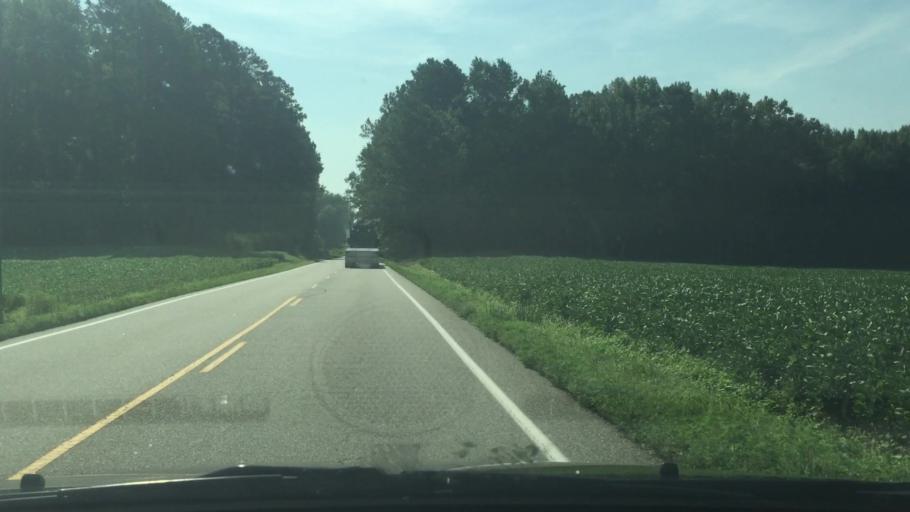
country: US
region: Virginia
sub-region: Prince George County
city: Prince George
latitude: 37.0728
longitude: -77.3452
